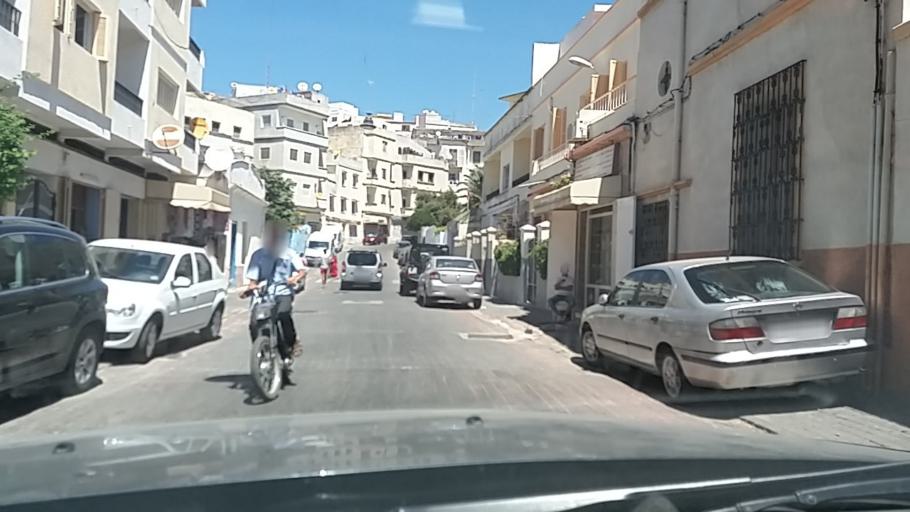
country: MA
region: Tanger-Tetouan
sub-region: Tanger-Assilah
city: Tangier
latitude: 35.7859
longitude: -5.8160
